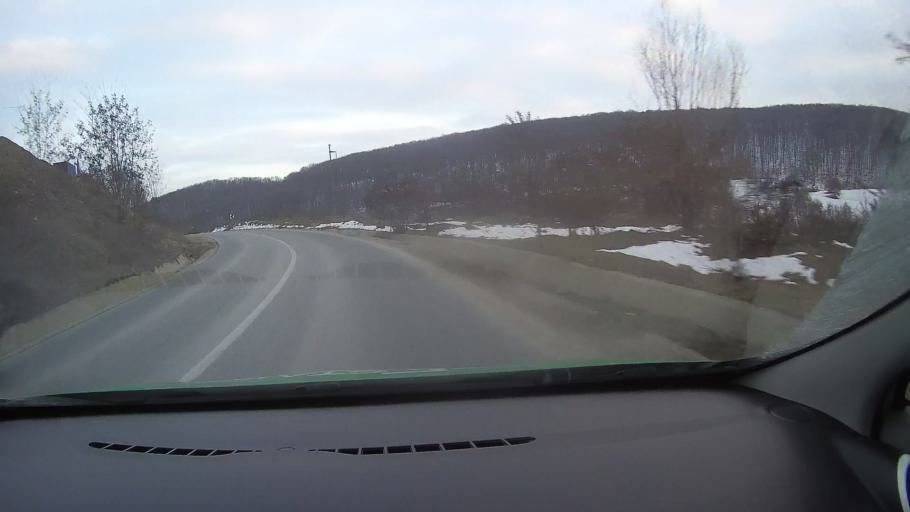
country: RO
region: Harghita
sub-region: Comuna Lupeni
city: Lupeni
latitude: 46.3581
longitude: 25.1916
